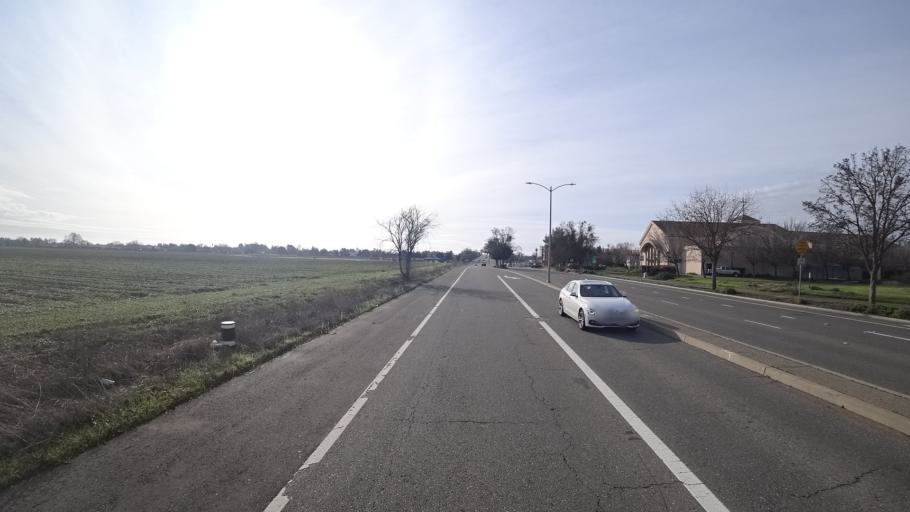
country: US
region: California
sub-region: Yolo County
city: Davis
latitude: 38.5585
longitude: -121.6941
